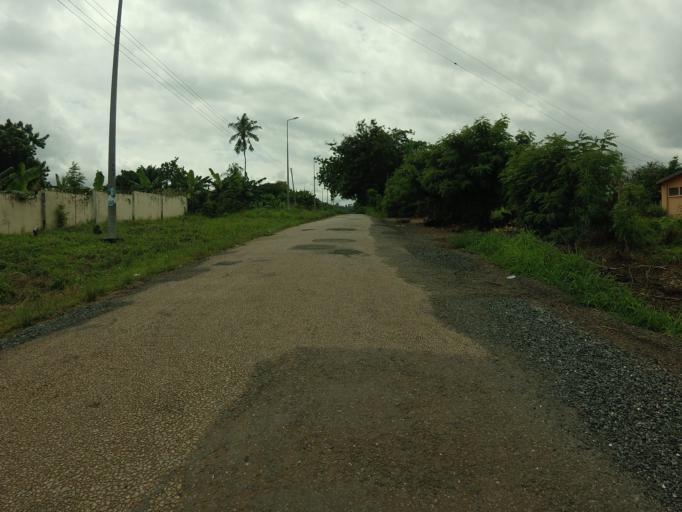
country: GH
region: Volta
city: Ho
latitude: 6.6050
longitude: 0.4619
